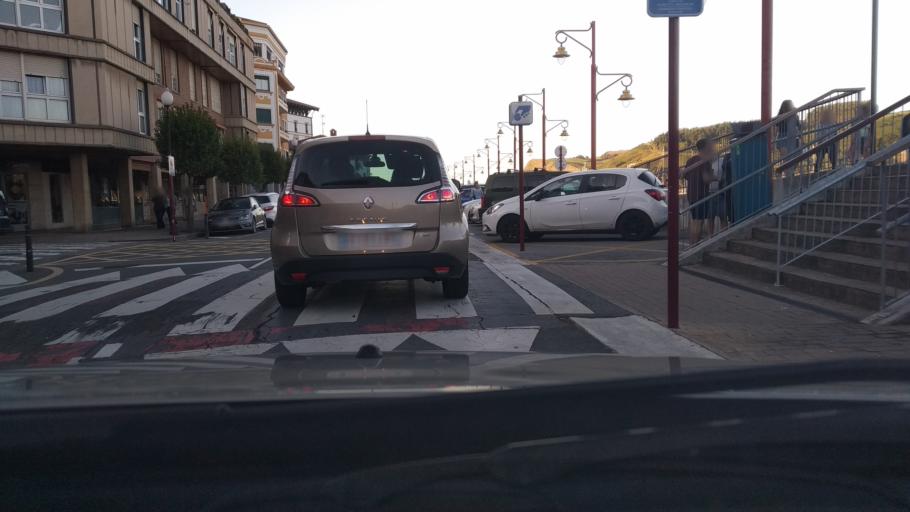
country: ES
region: Basque Country
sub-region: Provincia de Guipuzcoa
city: Zumaia
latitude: 43.2964
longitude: -2.2568
